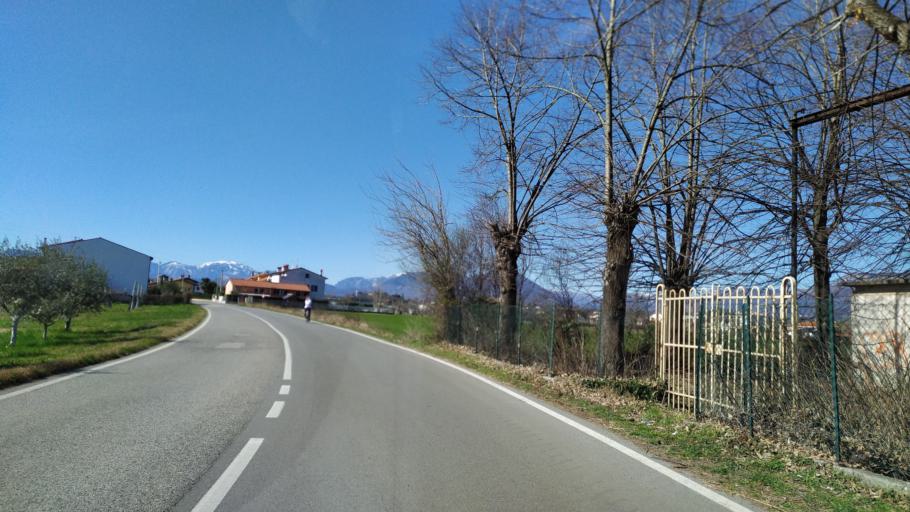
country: IT
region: Veneto
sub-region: Provincia di Vicenza
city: Breganze
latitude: 45.7017
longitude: 11.5583
